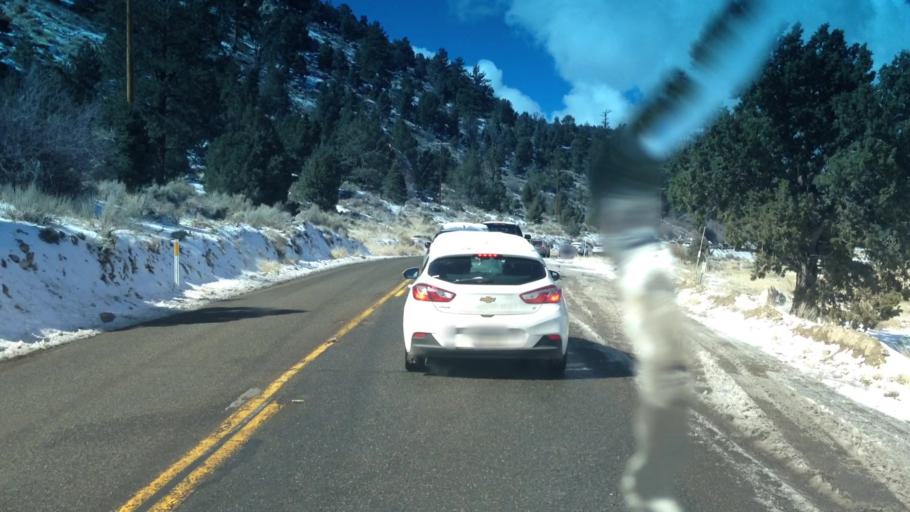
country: US
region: California
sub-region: San Bernardino County
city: Big Bear City
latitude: 34.2836
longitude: -116.8178
